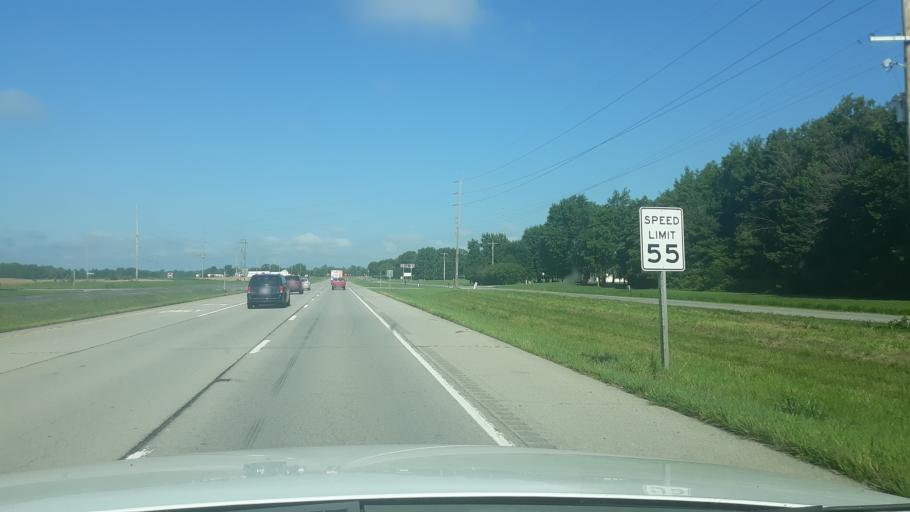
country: US
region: Illinois
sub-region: Williamson County
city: Marion
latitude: 37.7296
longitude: -88.8722
